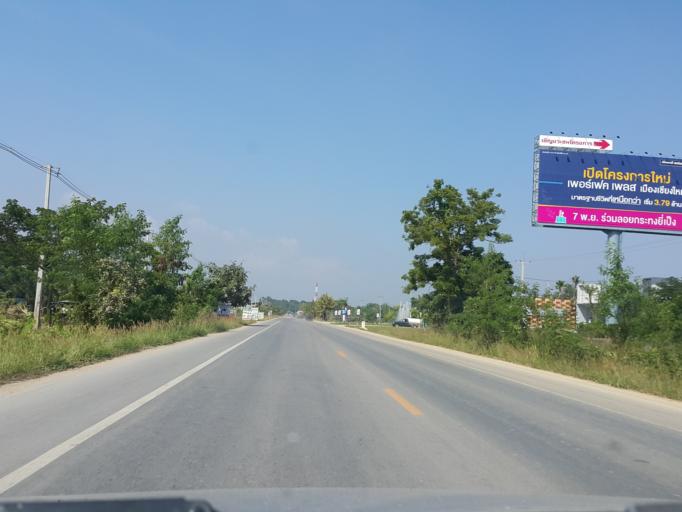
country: TH
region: Chiang Mai
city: San Sai
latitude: 18.8605
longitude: 98.9934
